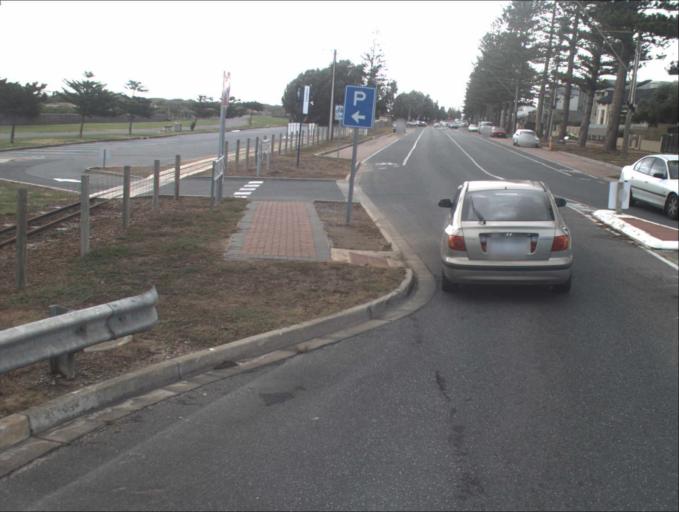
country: AU
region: South Australia
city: Port Adelaide
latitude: -34.8435
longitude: 138.4785
